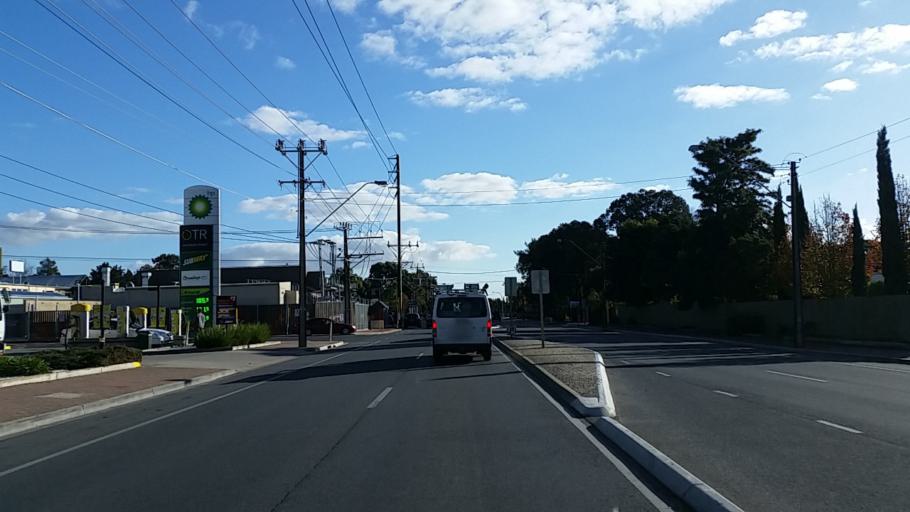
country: AU
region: South Australia
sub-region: Campbelltown
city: Paradise
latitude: -34.8763
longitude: 138.6740
